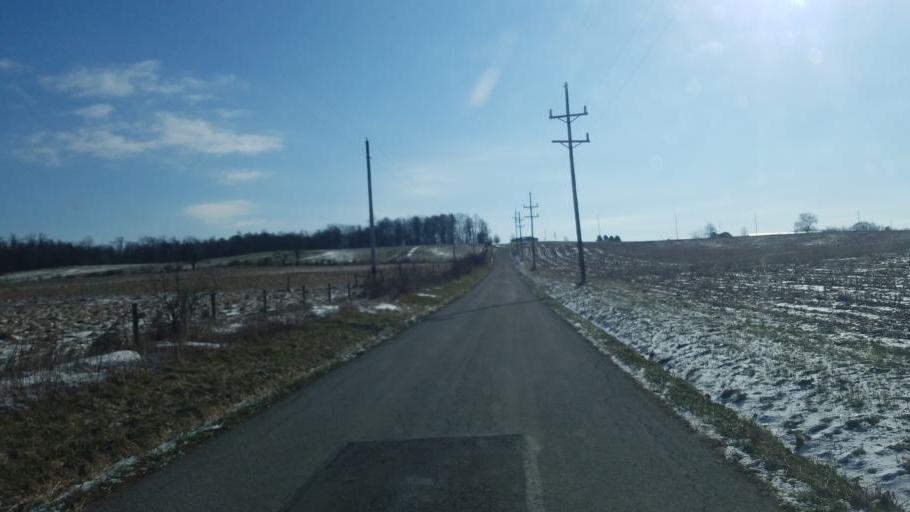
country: US
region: Ohio
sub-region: Knox County
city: Fredericktown
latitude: 40.5234
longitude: -82.4641
